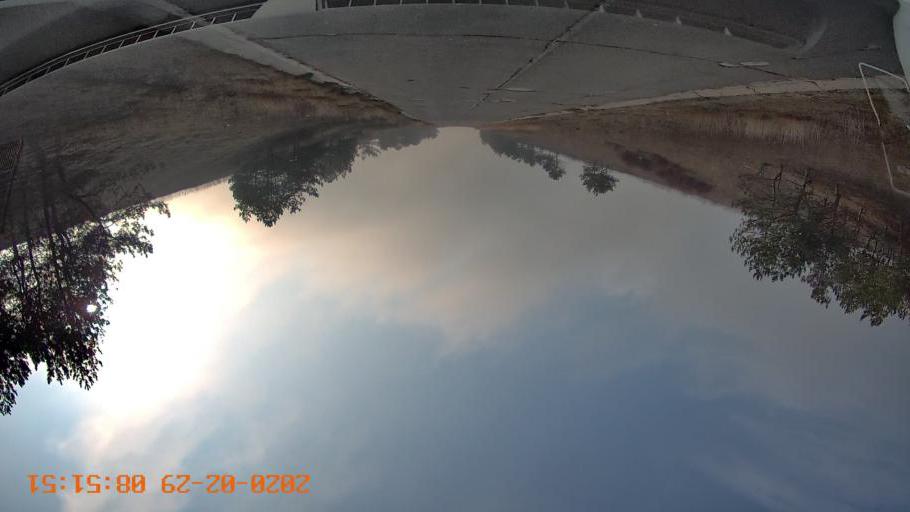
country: MD
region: Anenii Noi
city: Varnita
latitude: 46.9225
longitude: 29.5277
